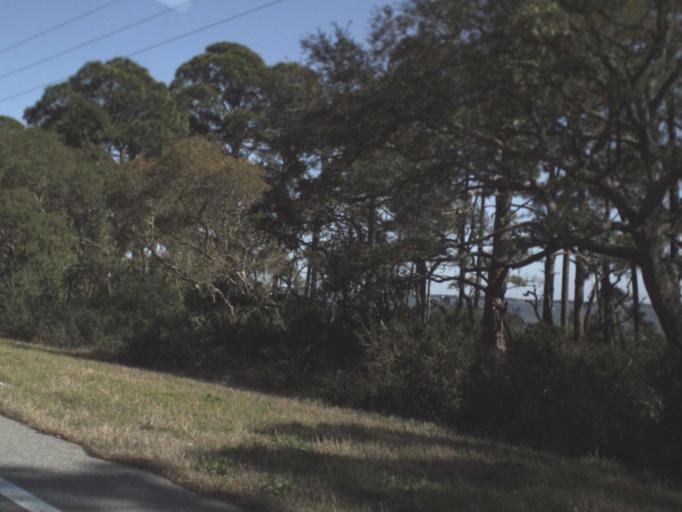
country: US
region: Florida
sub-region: Wakulla County
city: Crawfordville
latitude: 29.9224
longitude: -84.4072
